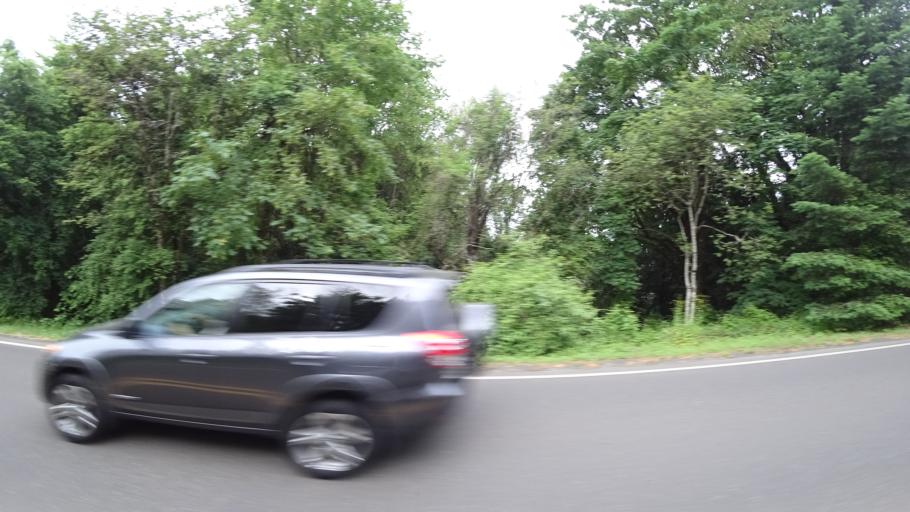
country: US
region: Oregon
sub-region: Washington County
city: Metzger
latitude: 45.4298
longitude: -122.7174
